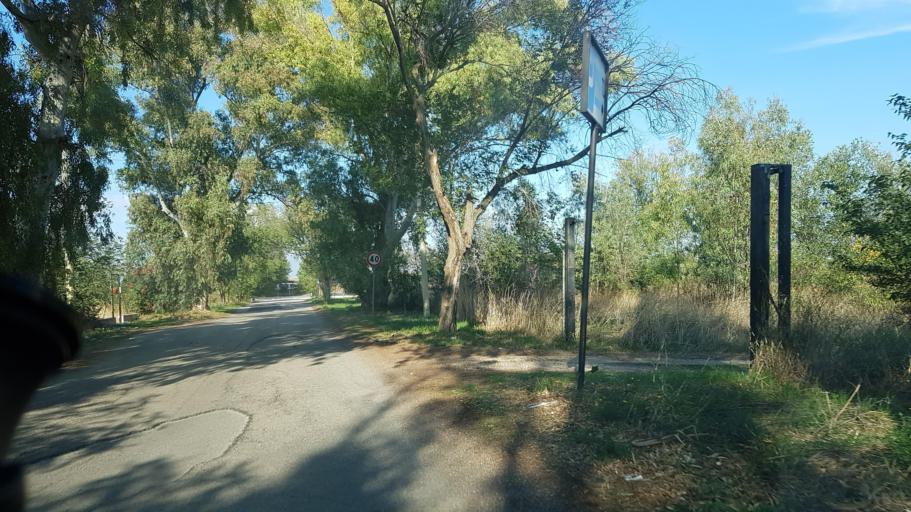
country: IT
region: Apulia
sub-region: Provincia di Foggia
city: Carapelle
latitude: 41.3984
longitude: 15.6525
